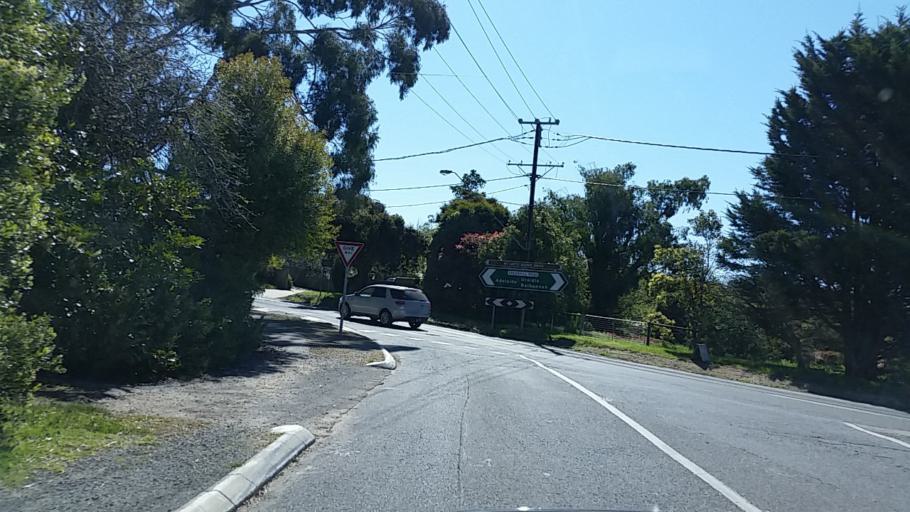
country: AU
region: South Australia
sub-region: Adelaide Hills
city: Bridgewater
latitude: -34.9598
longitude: 138.7344
